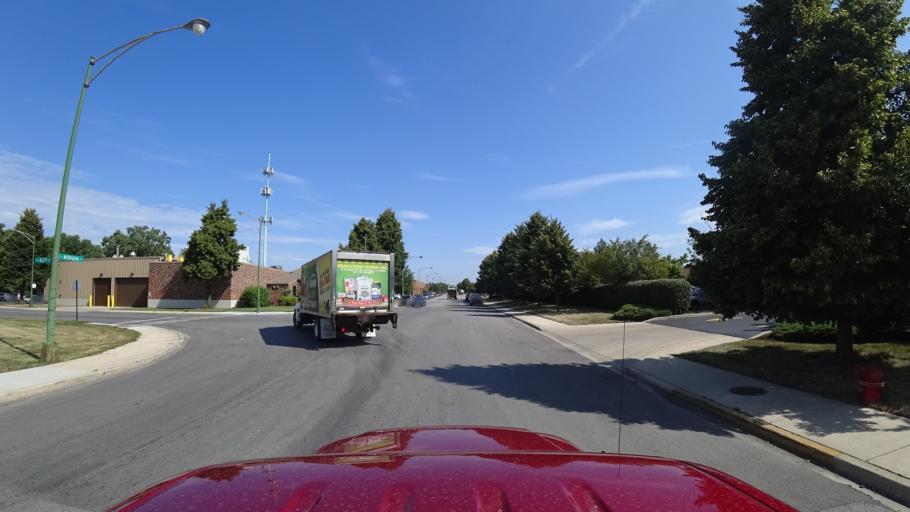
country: US
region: Illinois
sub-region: Cook County
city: Chicago
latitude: 41.8158
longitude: -87.6506
